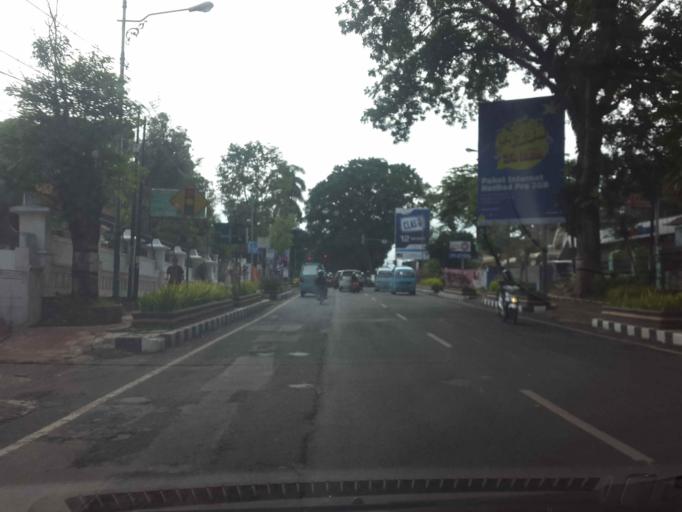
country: ID
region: Central Java
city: Salatiga
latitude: -7.3207
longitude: 110.4992
